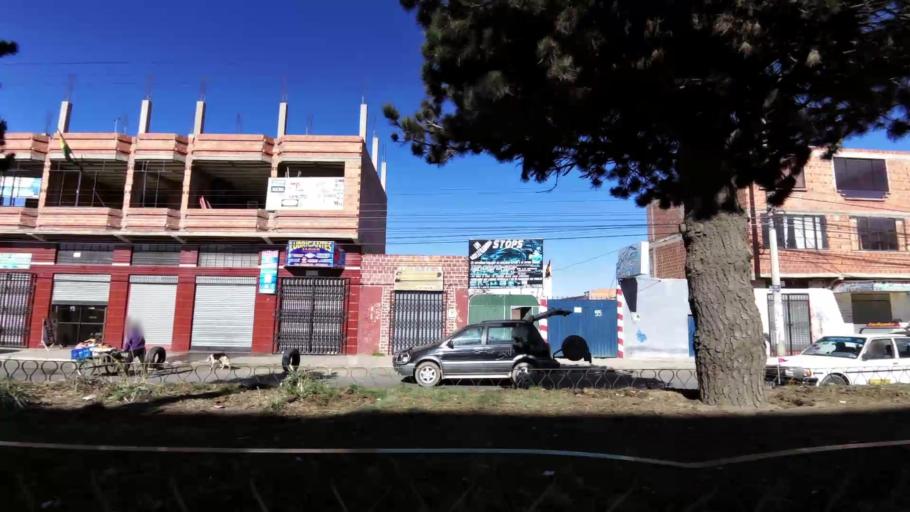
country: BO
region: La Paz
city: La Paz
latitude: -16.5277
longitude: -68.1978
